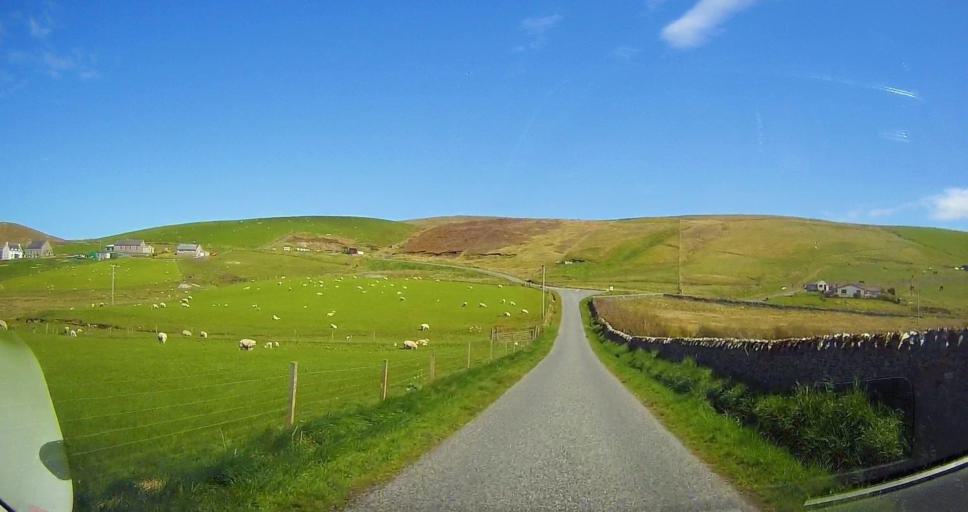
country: GB
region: Scotland
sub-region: Shetland Islands
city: Sandwick
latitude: 59.9725
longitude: -1.3180
